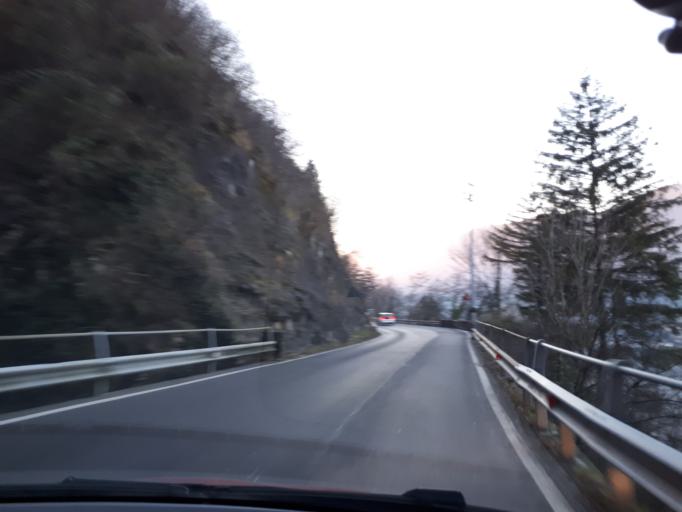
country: IT
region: Lombardy
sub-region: Provincia di Como
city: Faggeto Lario
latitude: 45.8569
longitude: 9.1406
